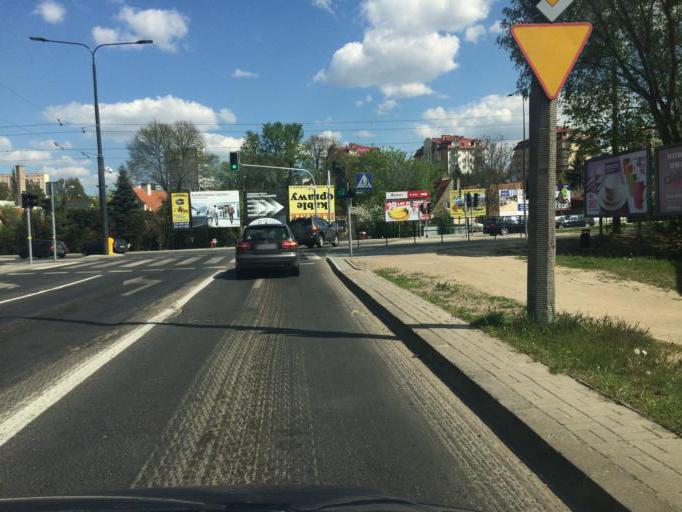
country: PL
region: Warmian-Masurian Voivodeship
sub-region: Powiat olsztynski
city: Olsztyn
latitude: 53.7645
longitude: 20.4852
